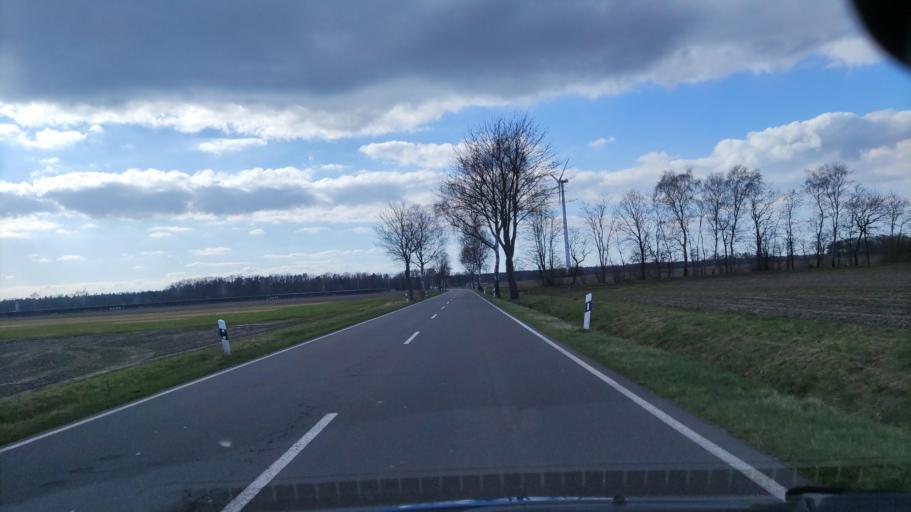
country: DE
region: Lower Saxony
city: Beedenbostel
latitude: 52.6370
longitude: 10.2387
